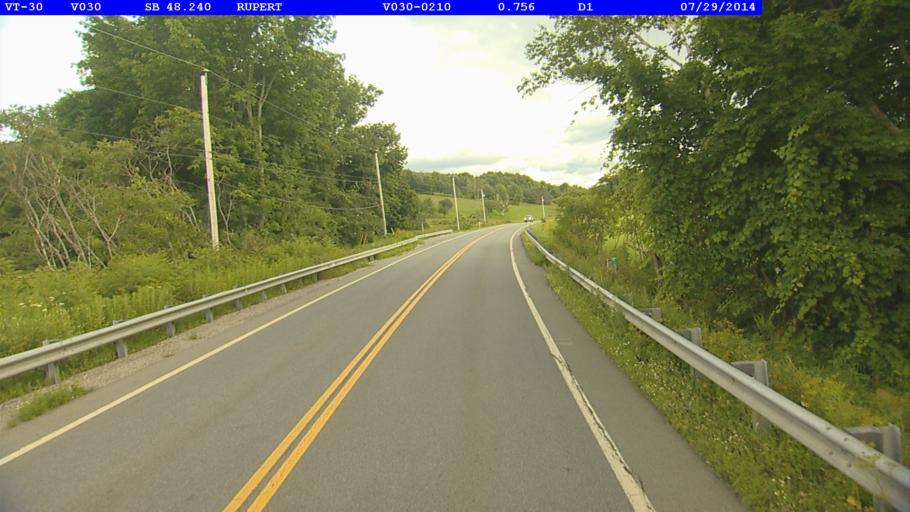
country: US
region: Vermont
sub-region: Bennington County
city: Manchester Center
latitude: 43.2814
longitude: -73.1263
